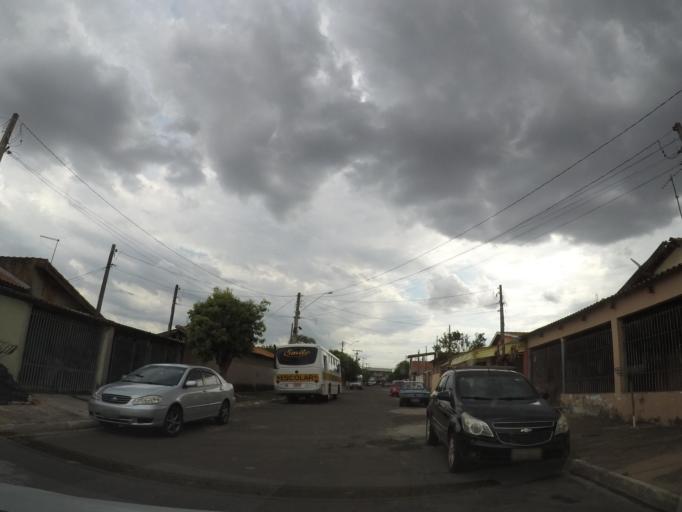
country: BR
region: Sao Paulo
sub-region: Sumare
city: Sumare
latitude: -22.8110
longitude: -47.2414
